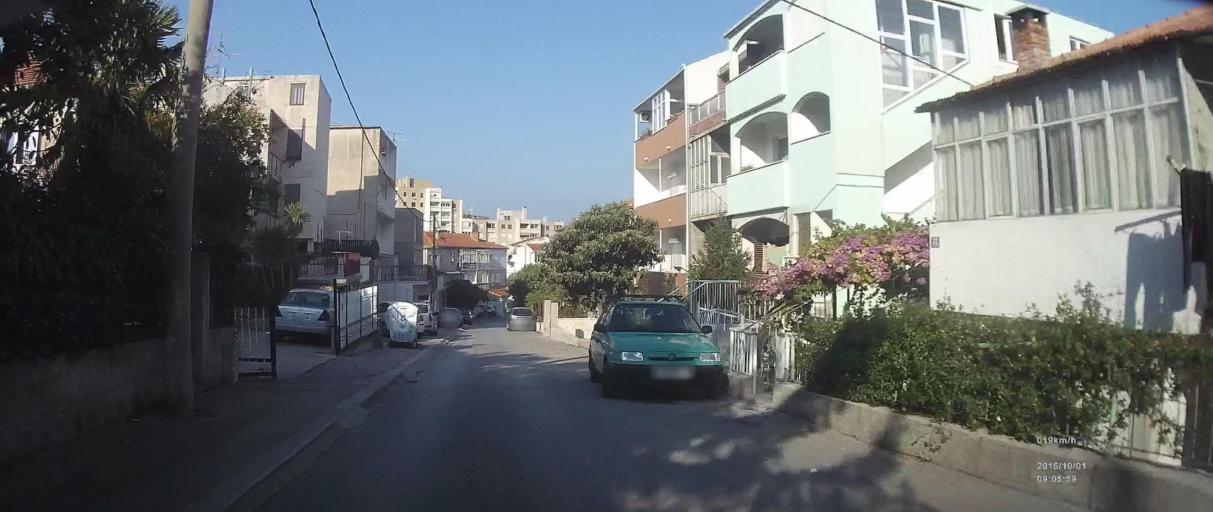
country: HR
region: Splitsko-Dalmatinska
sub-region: Grad Split
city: Split
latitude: 43.5180
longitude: 16.4527
